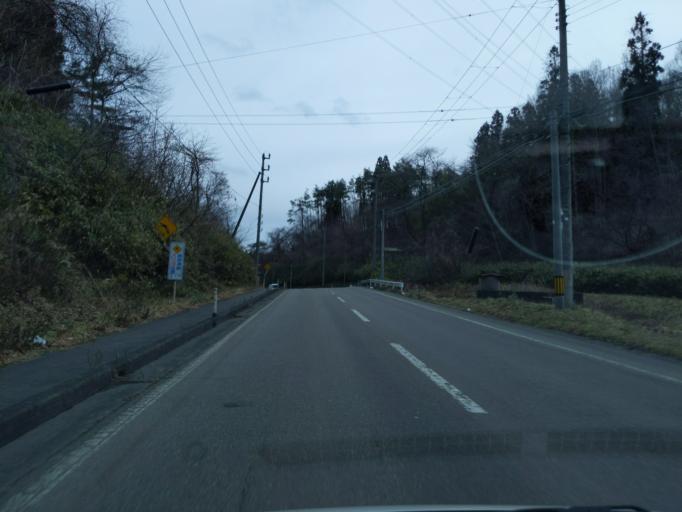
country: JP
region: Iwate
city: Mizusawa
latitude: 39.0308
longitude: 141.3035
